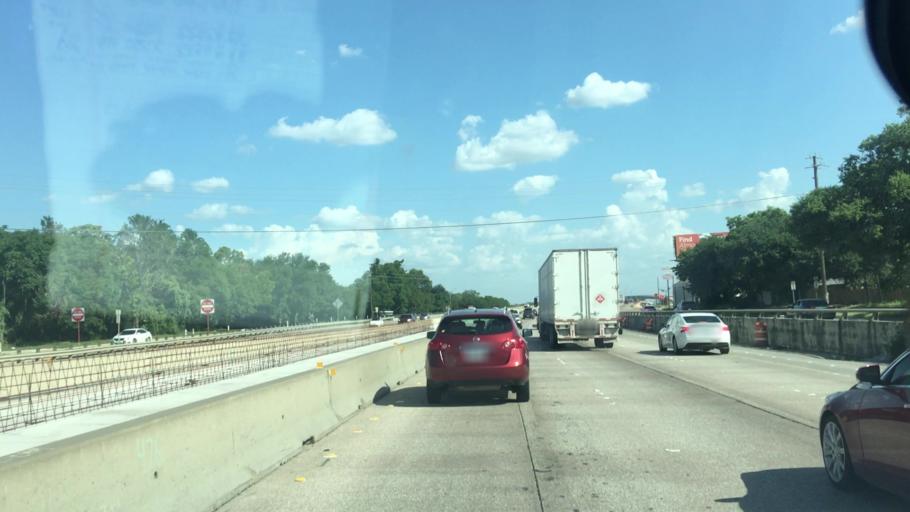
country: US
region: Texas
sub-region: Dallas County
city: Dallas
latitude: 32.7576
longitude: -96.7729
